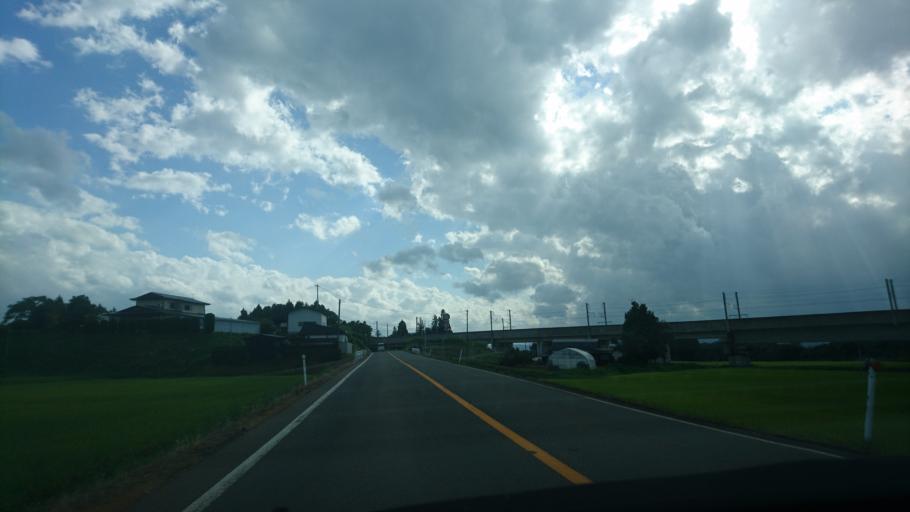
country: JP
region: Iwate
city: Hanamaki
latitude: 39.5087
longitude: 141.1753
